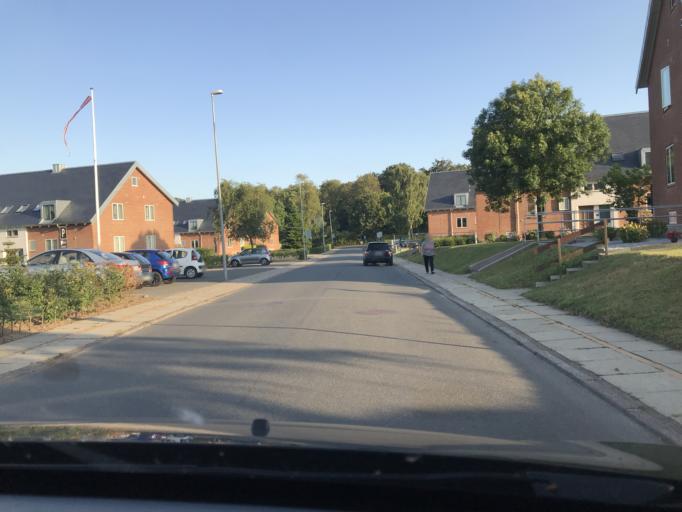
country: DK
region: South Denmark
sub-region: Vejle Kommune
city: Vejle
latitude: 55.7166
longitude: 9.5639
